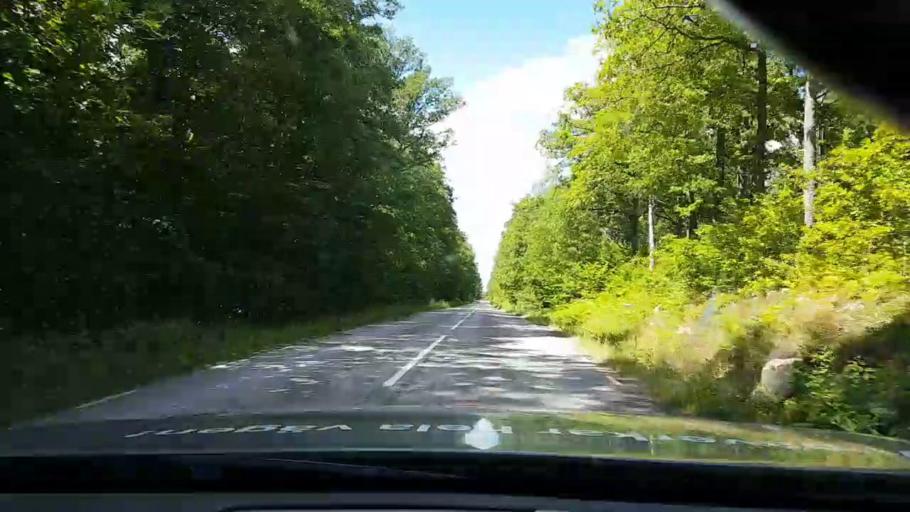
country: SE
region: Kalmar
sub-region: Vasterviks Kommun
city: Overum
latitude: 58.0690
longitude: 16.3894
